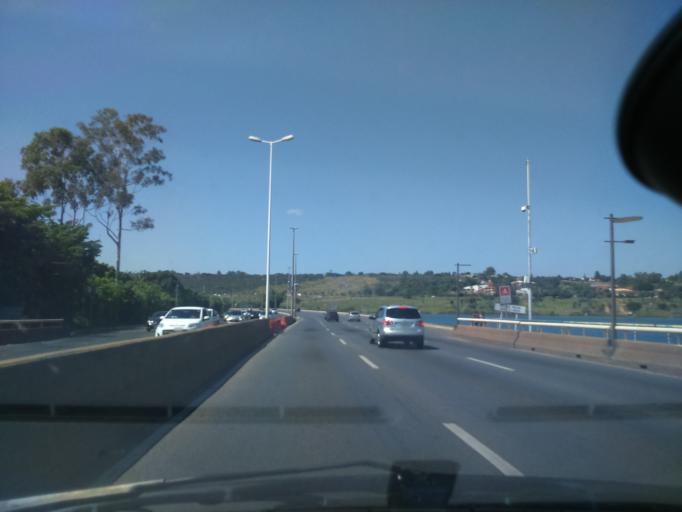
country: BR
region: Federal District
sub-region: Brasilia
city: Brasilia
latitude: -15.8286
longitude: -47.8272
